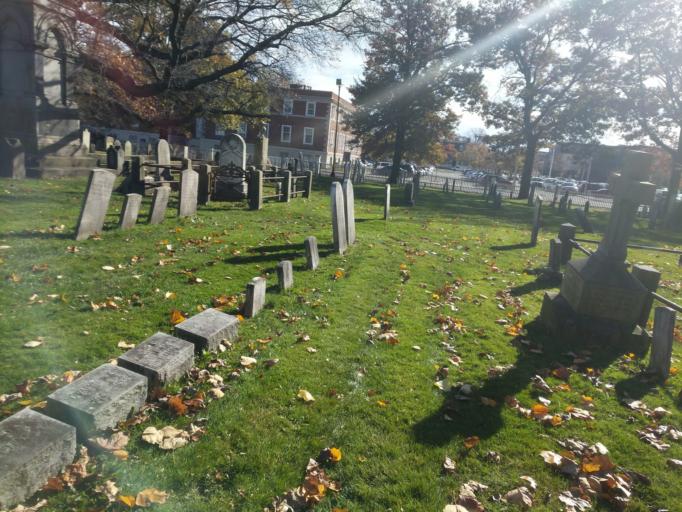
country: US
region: New York
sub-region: Nassau County
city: Hempstead
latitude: 40.7070
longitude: -73.6221
